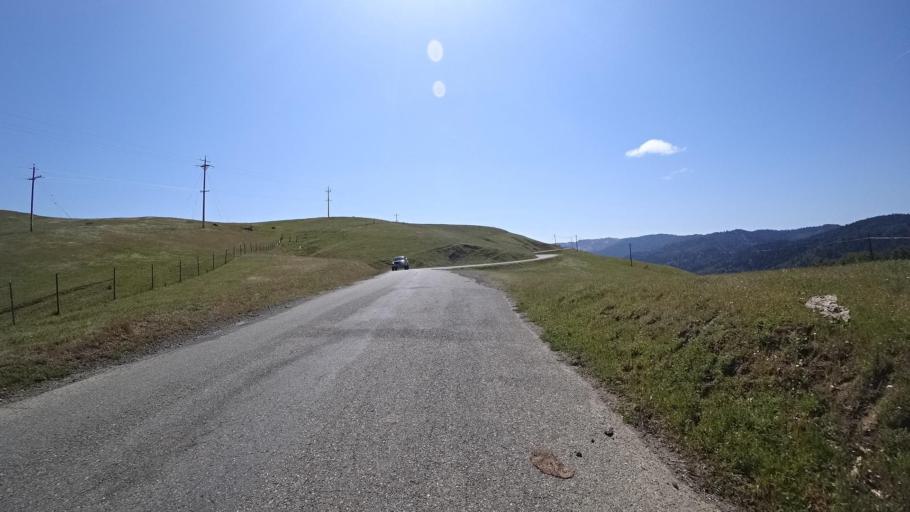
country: US
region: California
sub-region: Humboldt County
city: Redway
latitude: 40.0275
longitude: -123.6333
